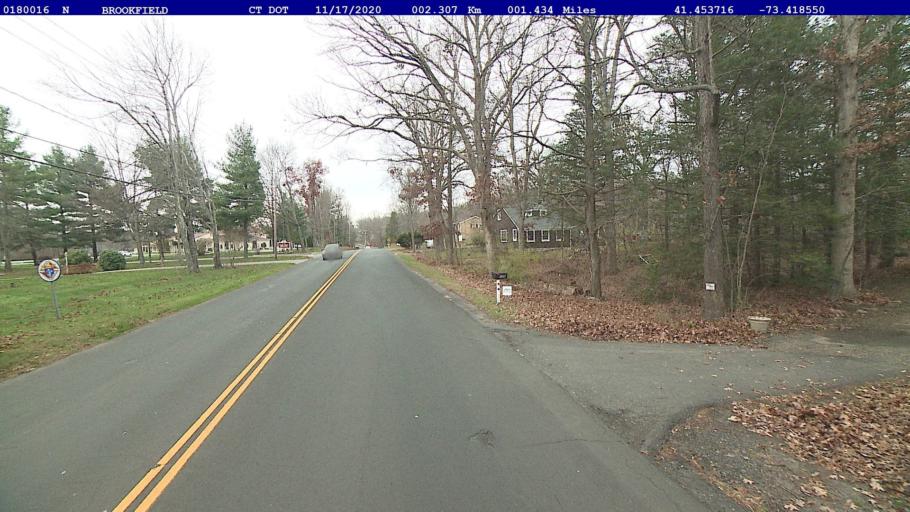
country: US
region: Connecticut
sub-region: Fairfield County
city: Danbury
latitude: 41.4537
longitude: -73.4186
